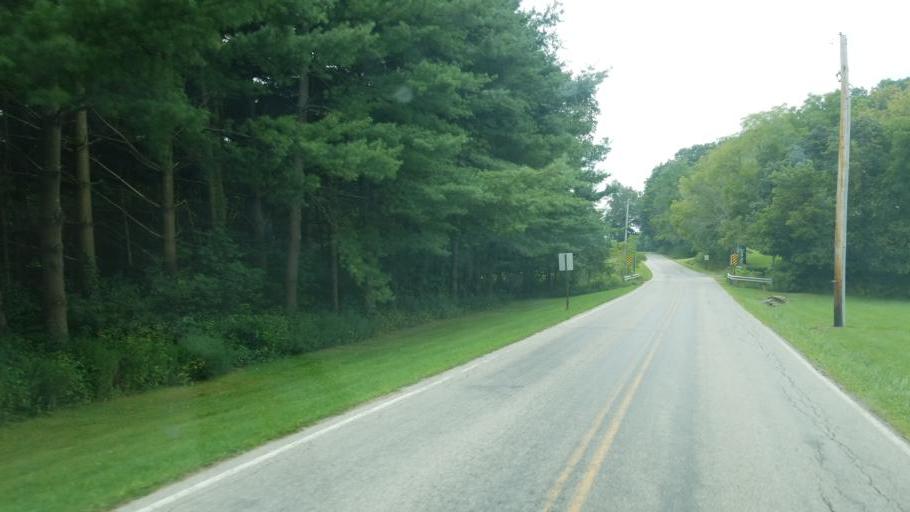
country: US
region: Ohio
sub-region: Sandusky County
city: Bellville
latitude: 40.6349
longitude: -82.4550
